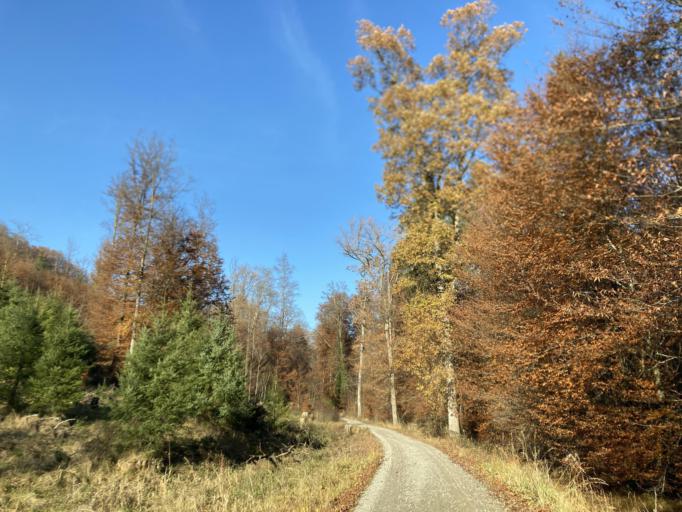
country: DE
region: Baden-Wuerttemberg
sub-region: Tuebingen Region
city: Tuebingen
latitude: 48.5695
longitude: 9.0329
